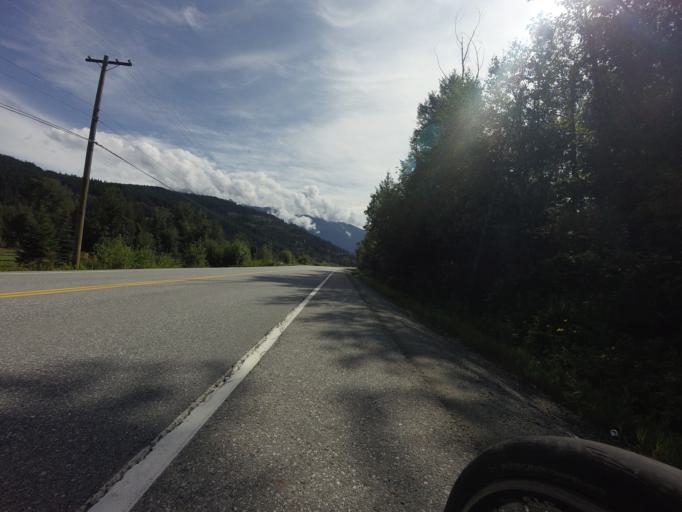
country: CA
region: British Columbia
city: Pemberton
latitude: 50.3118
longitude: -122.7523
